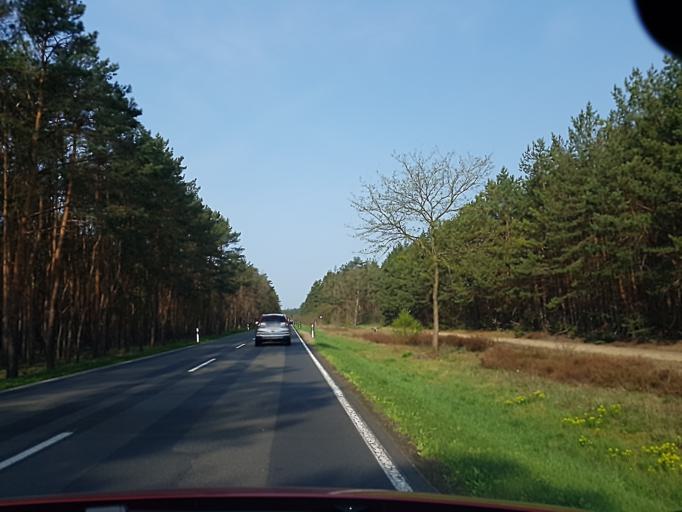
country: DE
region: Saxony
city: Beilrode
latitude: 51.5901
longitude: 13.1002
